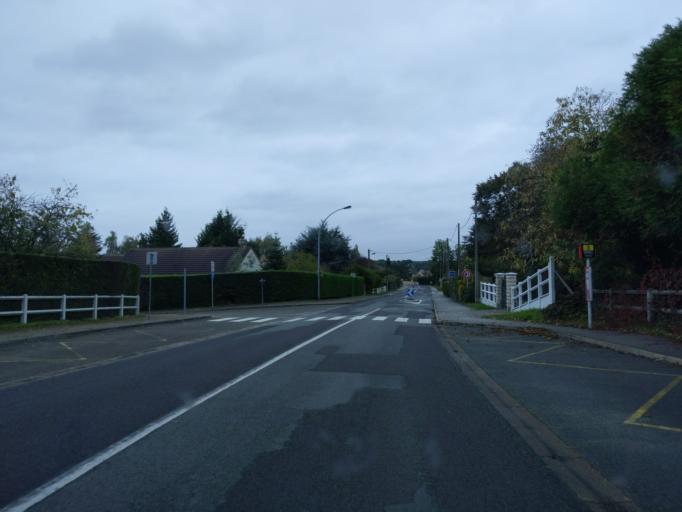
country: FR
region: Ile-de-France
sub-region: Departement des Yvelines
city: Saint-Arnoult-en-Yvelines
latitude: 48.5782
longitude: 1.9436
